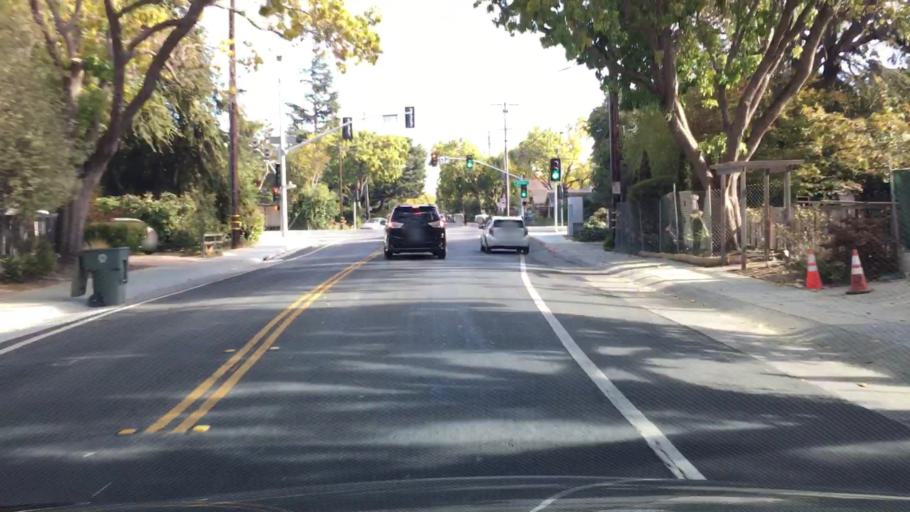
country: US
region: California
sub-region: Santa Clara County
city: Palo Alto
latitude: 37.4409
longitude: -122.1289
